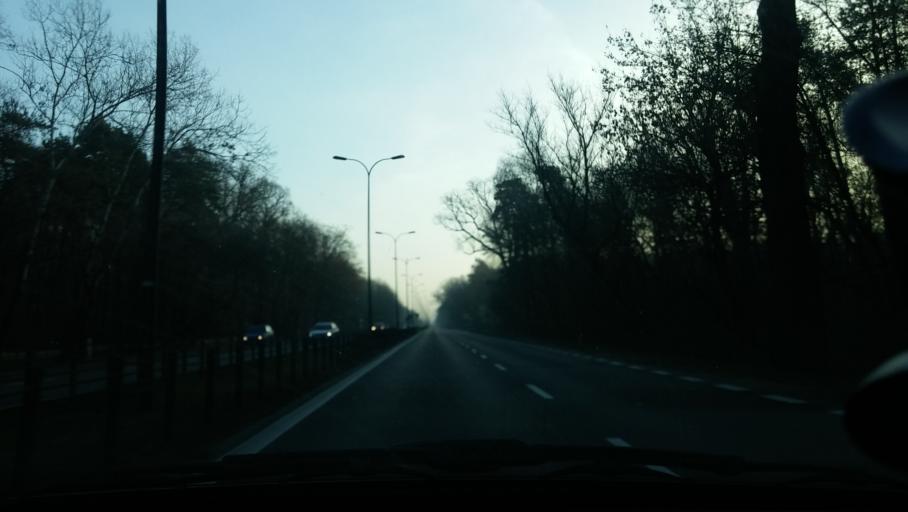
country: PL
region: Masovian Voivodeship
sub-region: Warszawa
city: Wawer
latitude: 52.2255
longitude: 21.1723
